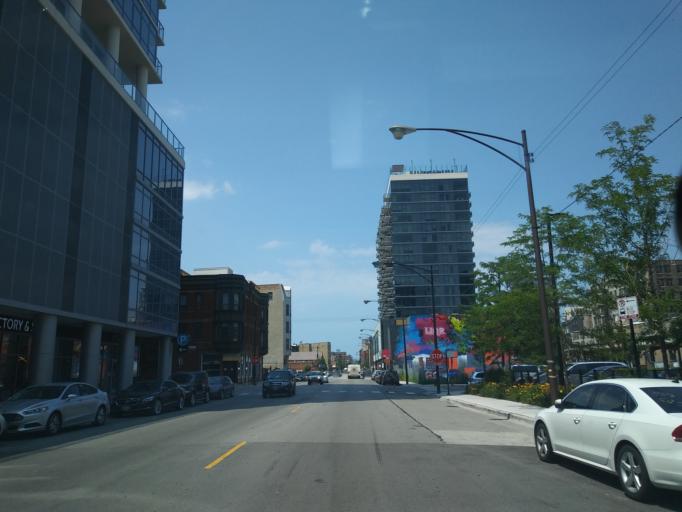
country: US
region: Illinois
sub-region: Cook County
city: Chicago
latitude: 41.8977
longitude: -87.6372
